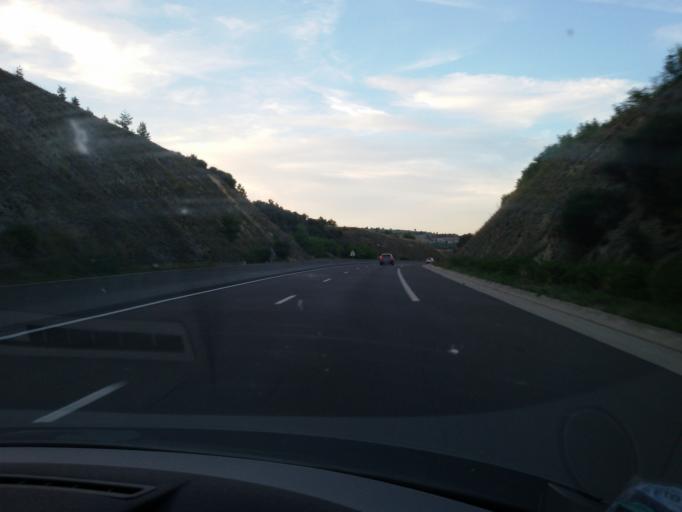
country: FR
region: Languedoc-Roussillon
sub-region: Departement de la Lozere
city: Chirac
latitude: 44.5222
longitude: 3.2408
